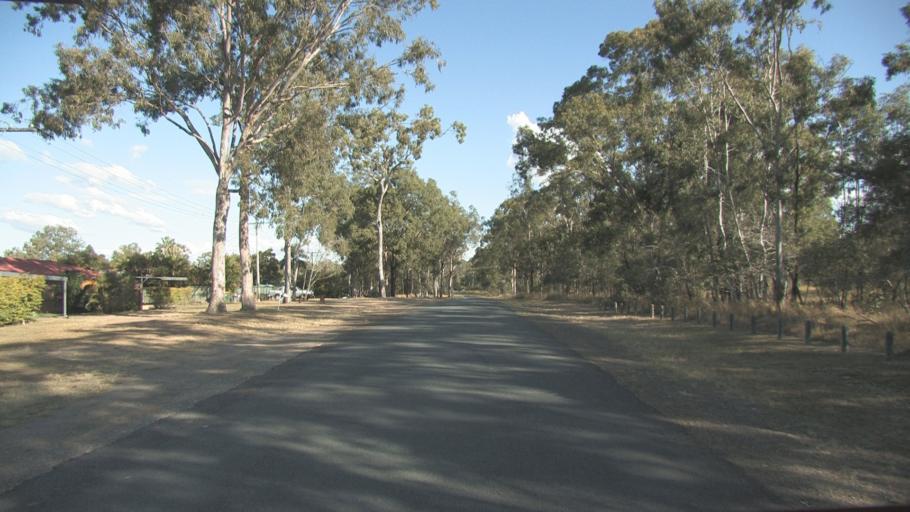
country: AU
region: Queensland
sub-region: Logan
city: Park Ridge South
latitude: -27.7207
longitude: 152.9856
